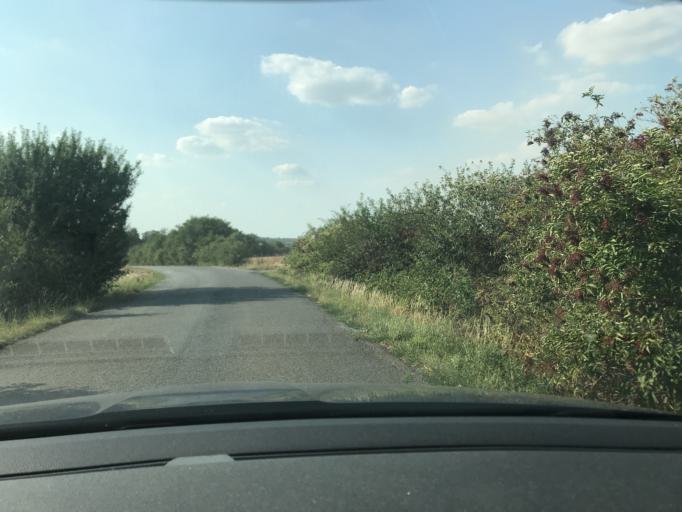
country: CZ
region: Central Bohemia
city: Kralupy nad Vltavou
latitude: 50.2315
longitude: 14.3157
